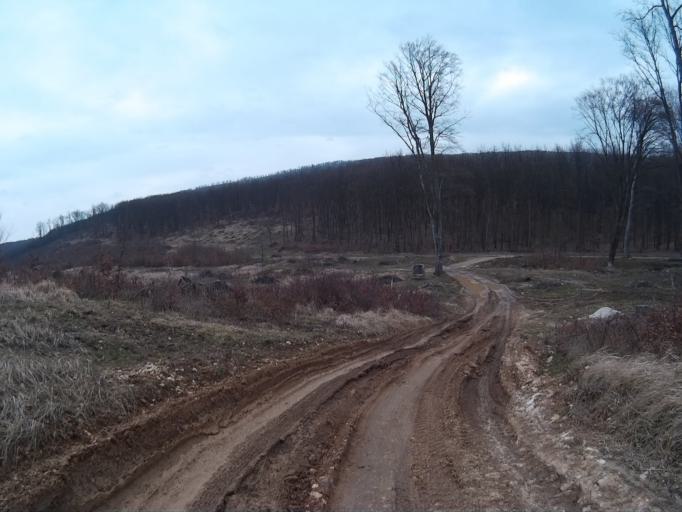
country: HU
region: Veszprem
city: Zirc
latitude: 47.1878
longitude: 17.8984
